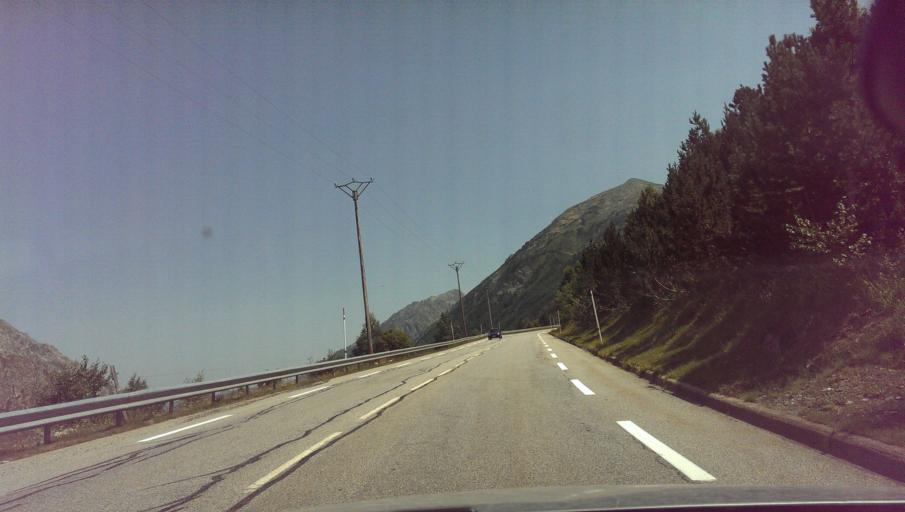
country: AD
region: Encamp
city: Pas de la Casa
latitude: 42.5663
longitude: 1.7837
